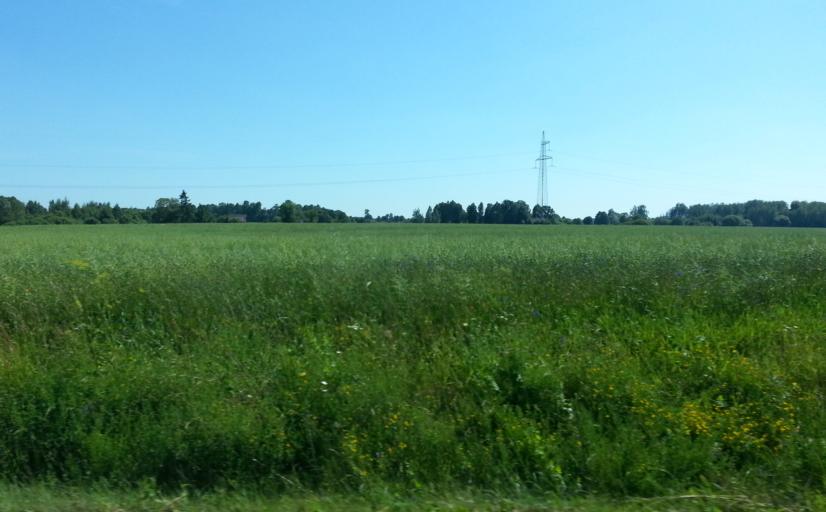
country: LT
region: Panevezys
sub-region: Birzai
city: Birzai
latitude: 56.2154
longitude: 24.6549
